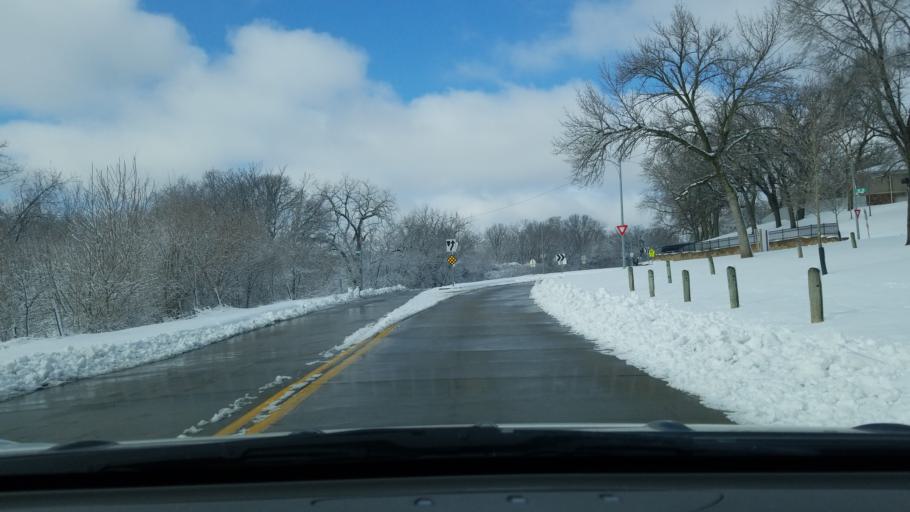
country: US
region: Nebraska
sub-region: Douglas County
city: Omaha
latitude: 41.2199
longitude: -95.9377
